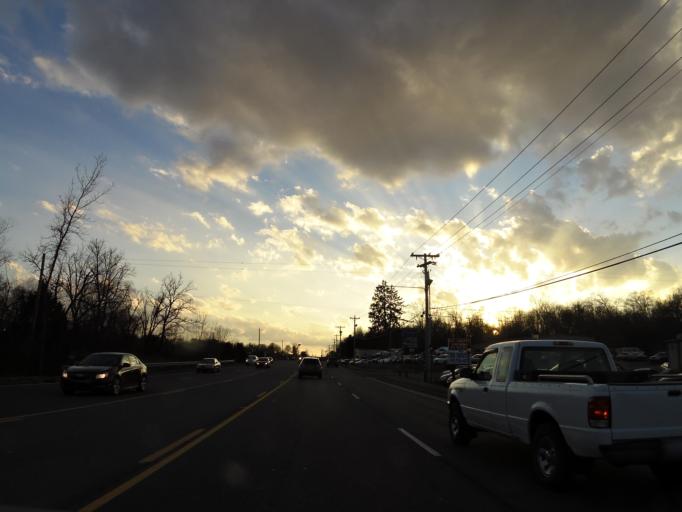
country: US
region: Tennessee
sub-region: Wilson County
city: Green Hill
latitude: 36.2279
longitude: -86.5366
